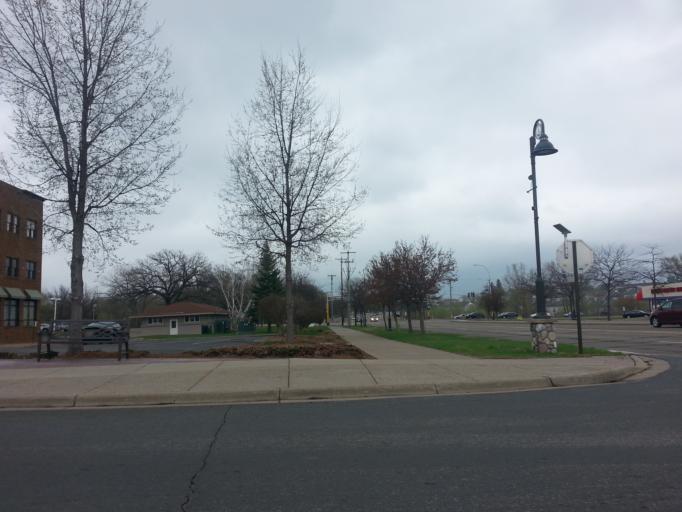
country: US
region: Minnesota
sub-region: Scott County
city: Prior Lake
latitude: 44.7139
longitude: -93.4243
